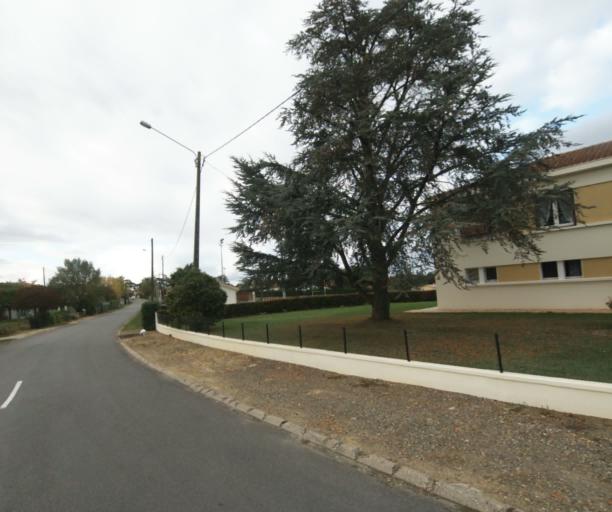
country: FR
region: Midi-Pyrenees
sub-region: Departement du Gers
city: Eauze
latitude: 43.9447
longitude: 0.0938
